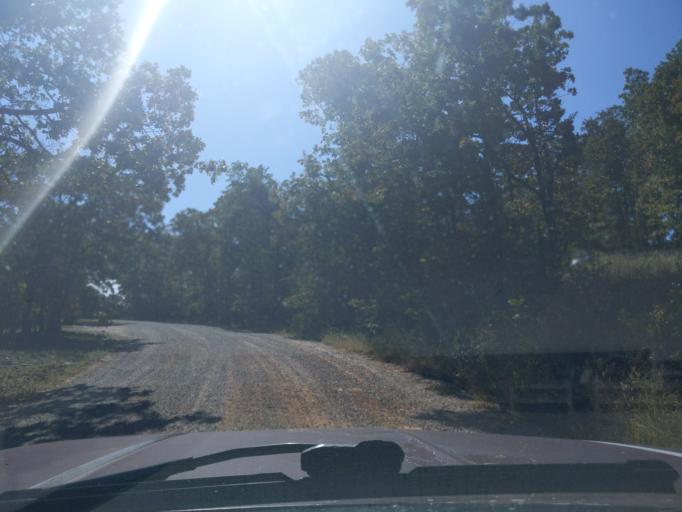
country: US
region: Oklahoma
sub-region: Creek County
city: Bristow
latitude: 35.6785
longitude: -96.4234
